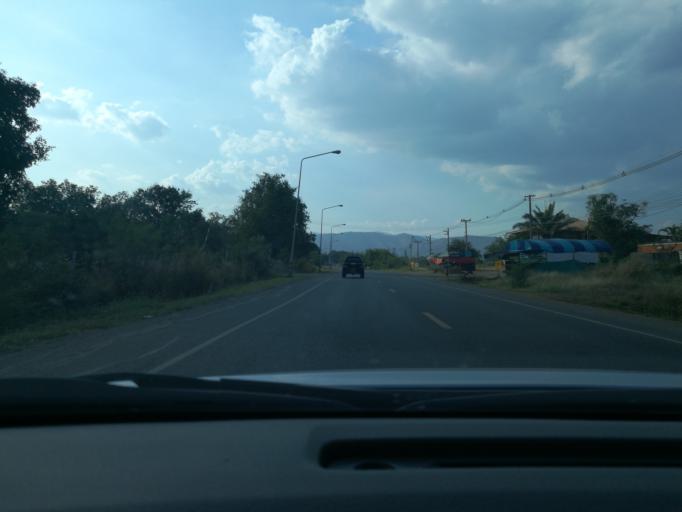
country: TH
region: Phetchabun
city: Phetchabun
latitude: 16.5405
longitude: 101.1526
